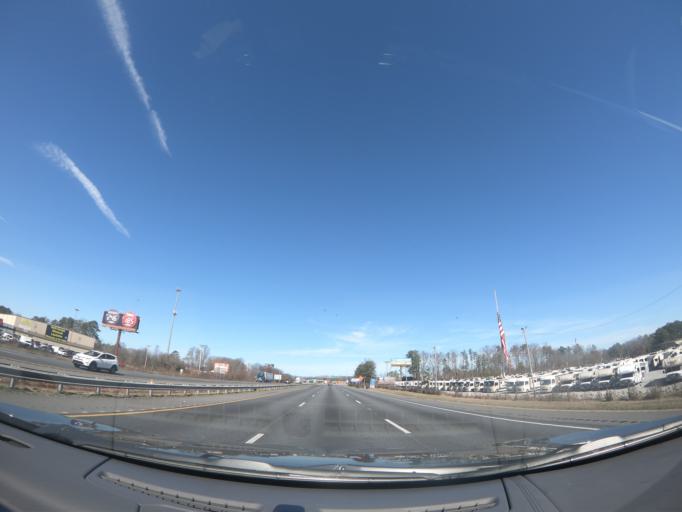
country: US
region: Georgia
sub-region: Catoosa County
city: Indian Springs
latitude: 34.9840
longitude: -85.2006
